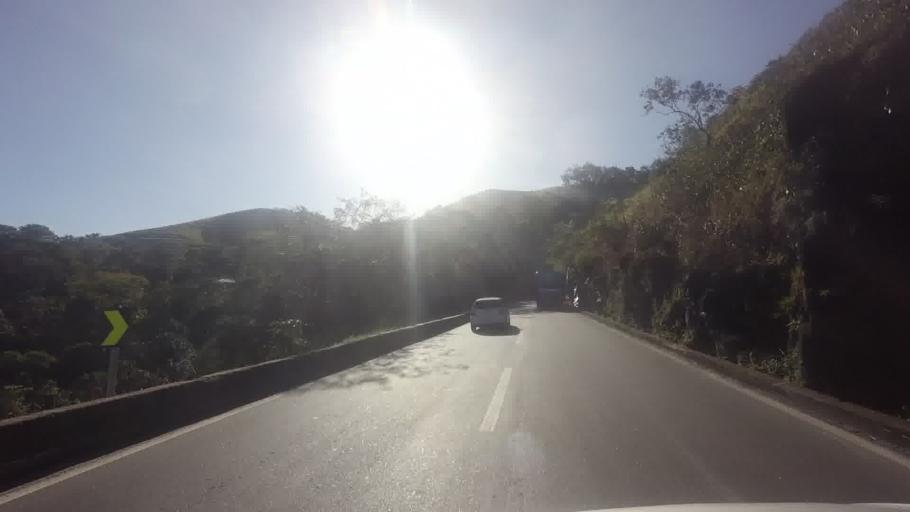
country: BR
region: Rio de Janeiro
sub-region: Petropolis
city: Petropolis
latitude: -22.5910
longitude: -43.2748
